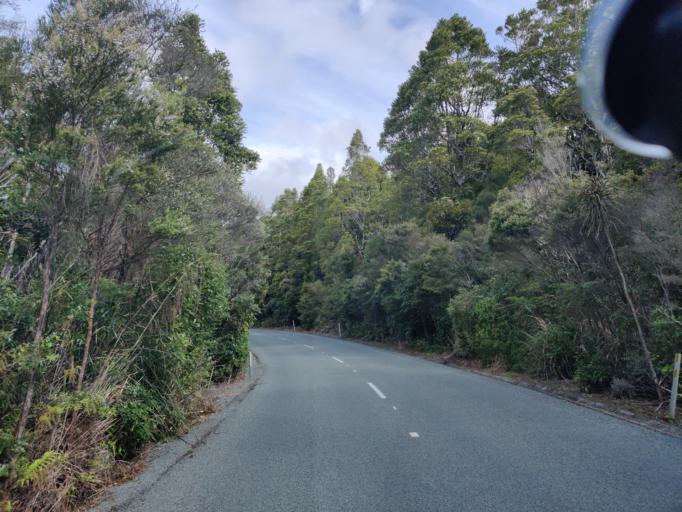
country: NZ
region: Northland
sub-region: Far North District
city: Waimate North
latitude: -35.6105
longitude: 173.5429
